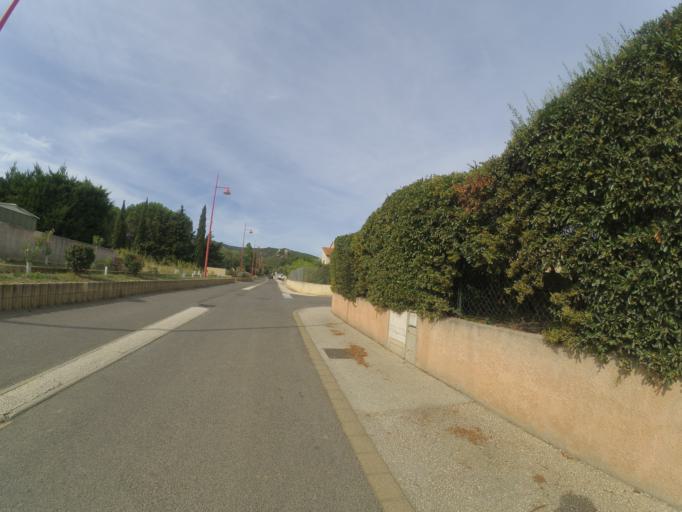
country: FR
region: Languedoc-Roussillon
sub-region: Departement des Pyrenees-Orientales
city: Millas
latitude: 42.6562
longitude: 2.6698
